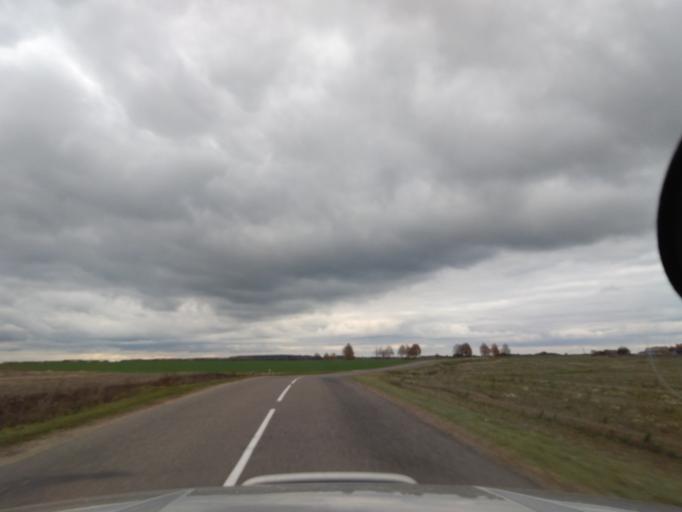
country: BY
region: Minsk
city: Slutsk
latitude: 53.2033
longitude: 27.3635
